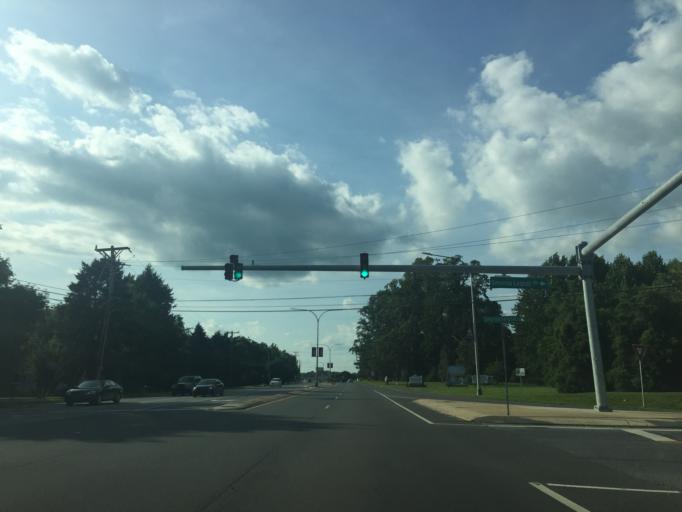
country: US
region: Delaware
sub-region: Kent County
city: Smyrna
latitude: 39.2911
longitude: -75.5964
